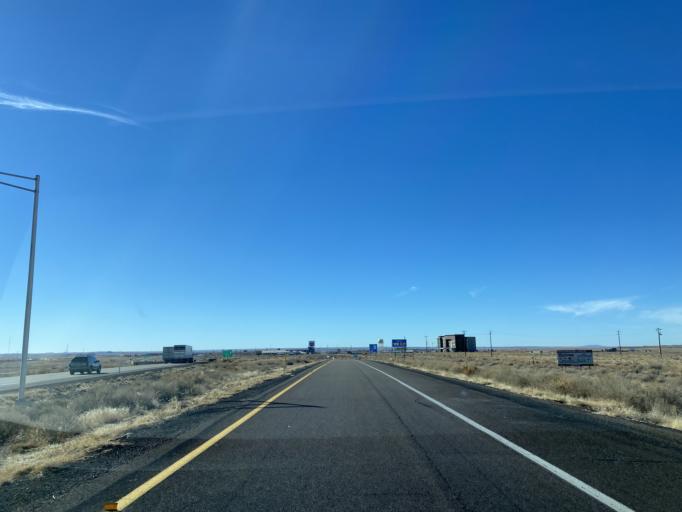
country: US
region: Arizona
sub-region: Navajo County
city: Holbrook
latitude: 34.9420
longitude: -110.1274
